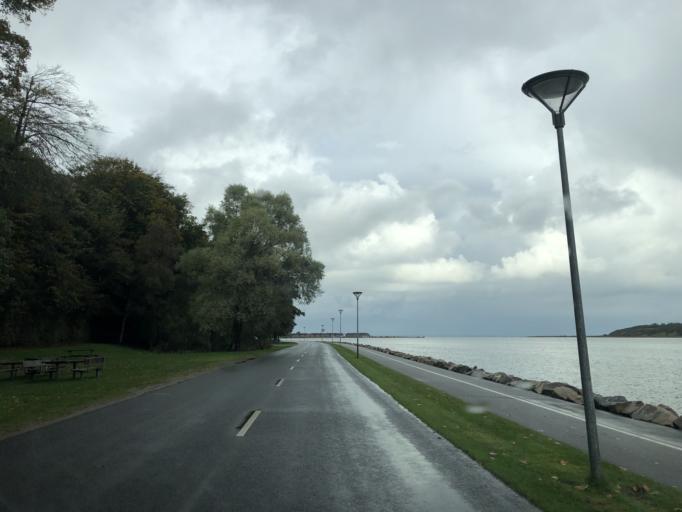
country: DK
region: Central Jutland
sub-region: Lemvig Kommune
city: Lemvig
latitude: 56.5546
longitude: 8.2959
